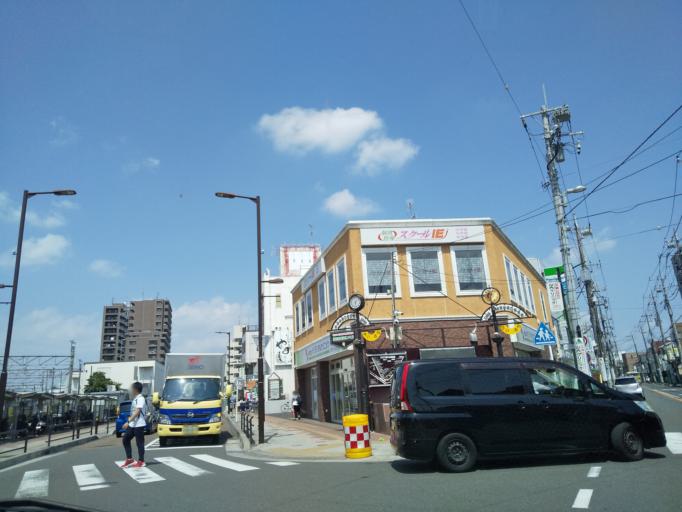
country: JP
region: Kanagawa
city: Zama
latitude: 35.4989
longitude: 139.4088
